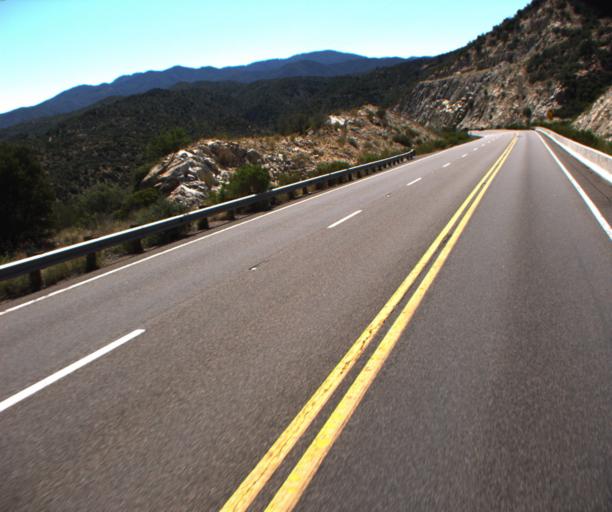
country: US
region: Arizona
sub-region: Gila County
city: Miami
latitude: 33.3645
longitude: -110.9609
